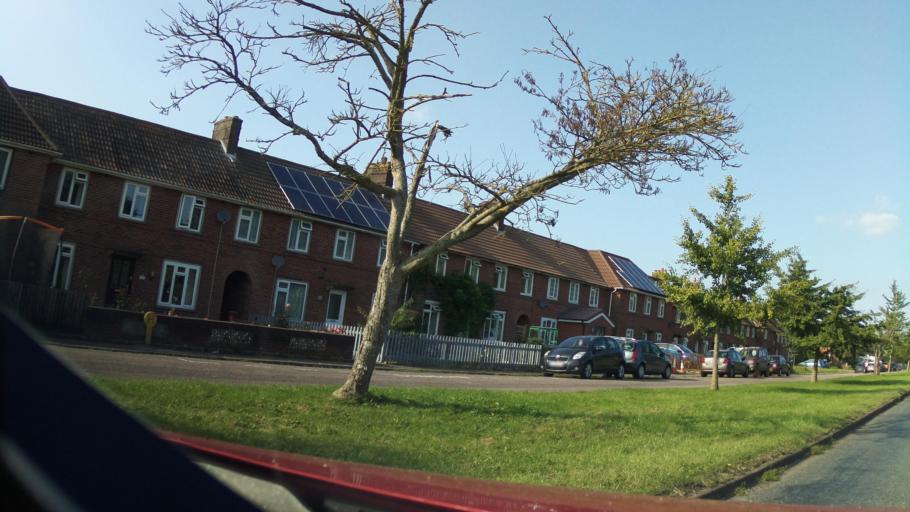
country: GB
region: England
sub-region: Devon
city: Tiverton
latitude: 50.8950
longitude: -3.4932
